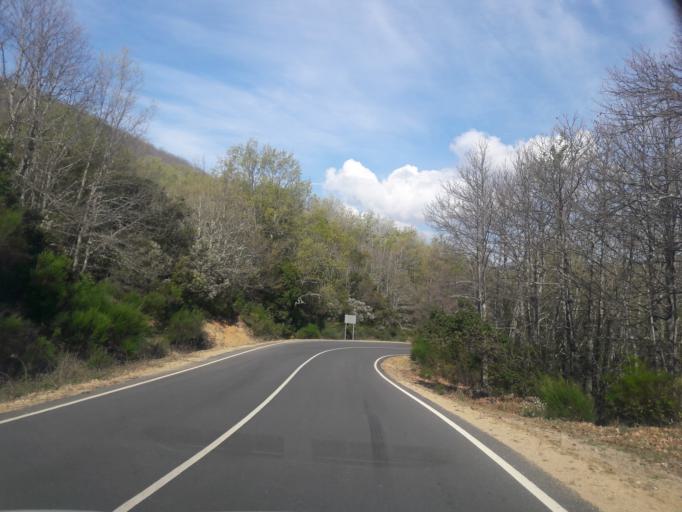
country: ES
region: Castille and Leon
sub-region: Provincia de Salamanca
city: Santibanez de la Sierra
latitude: 40.4909
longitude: -5.9227
